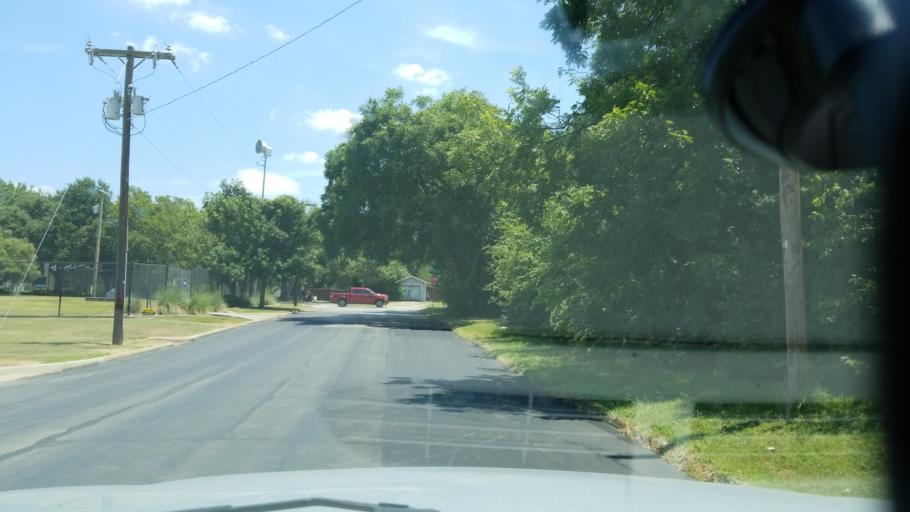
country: US
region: Texas
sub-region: Dallas County
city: Grand Prairie
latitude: 32.7553
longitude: -96.9639
